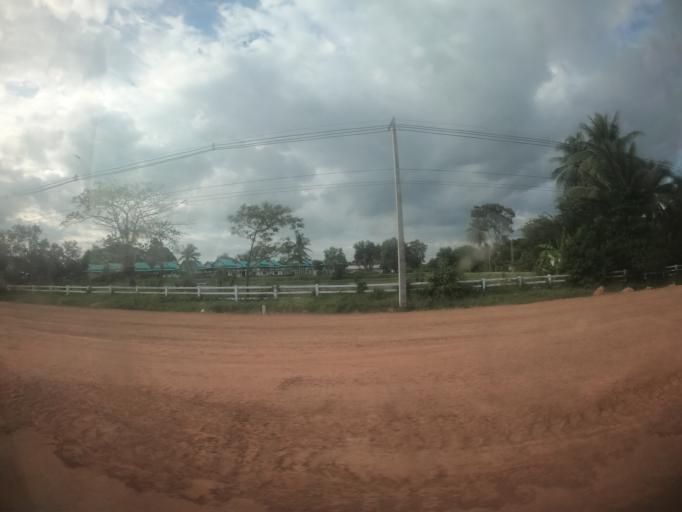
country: TH
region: Surin
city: Kap Choeng
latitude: 14.4707
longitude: 103.6164
